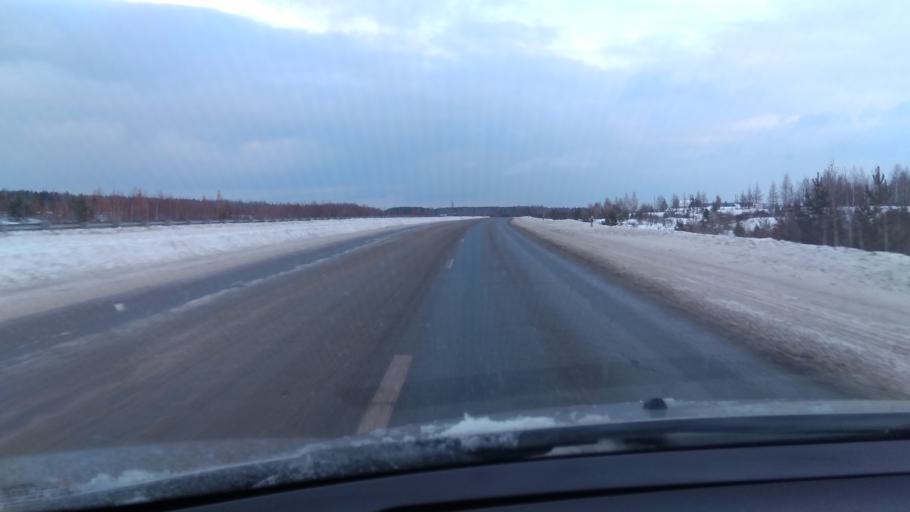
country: RU
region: Sverdlovsk
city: Nev'yansk
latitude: 57.5181
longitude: 60.1814
